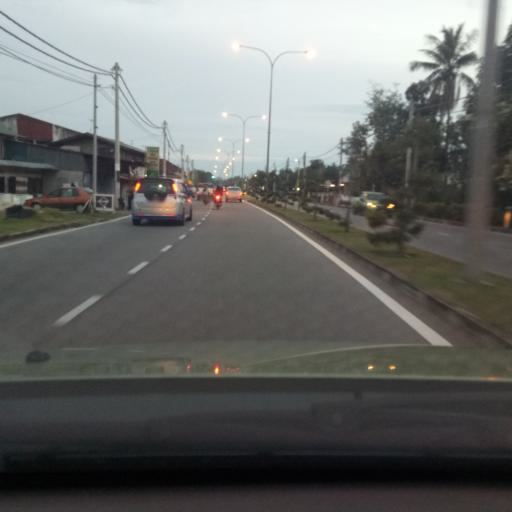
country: MY
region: Kedah
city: Alor Setar
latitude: 6.1162
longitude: 100.3754
